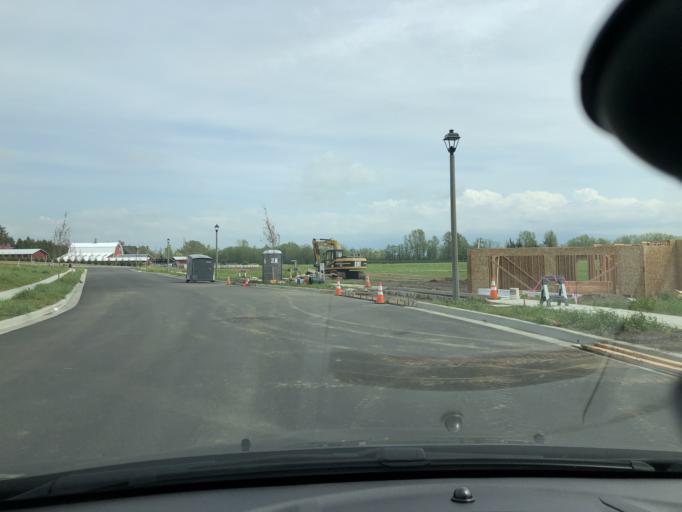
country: US
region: Washington
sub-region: Whatcom County
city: Lynden
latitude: 48.9343
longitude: -122.4691
